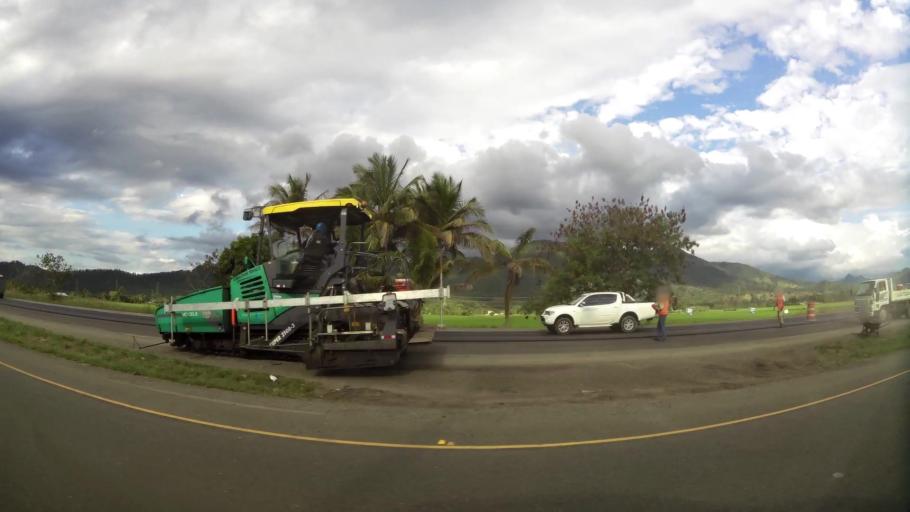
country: DO
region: Monsenor Nouel
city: Bonao
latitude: 18.8989
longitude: -70.3701
